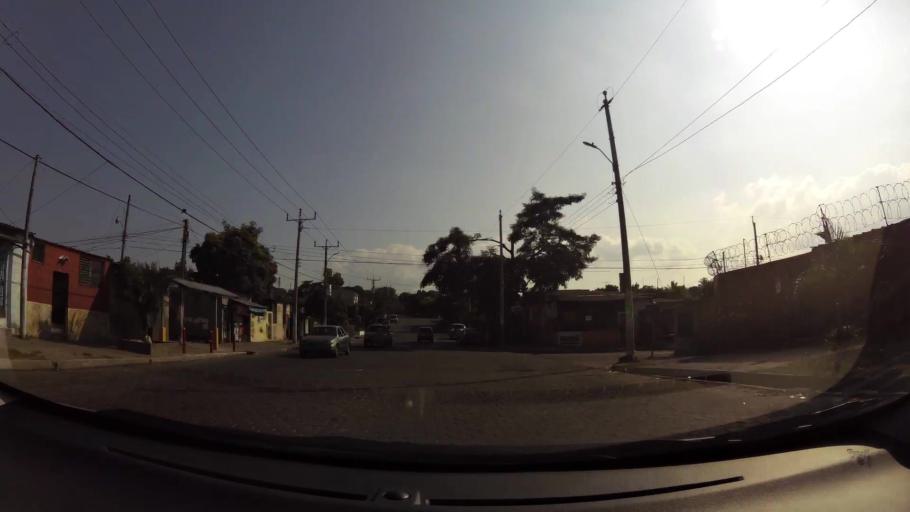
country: SV
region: San Salvador
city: Ilopango
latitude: 13.7156
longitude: -89.1074
